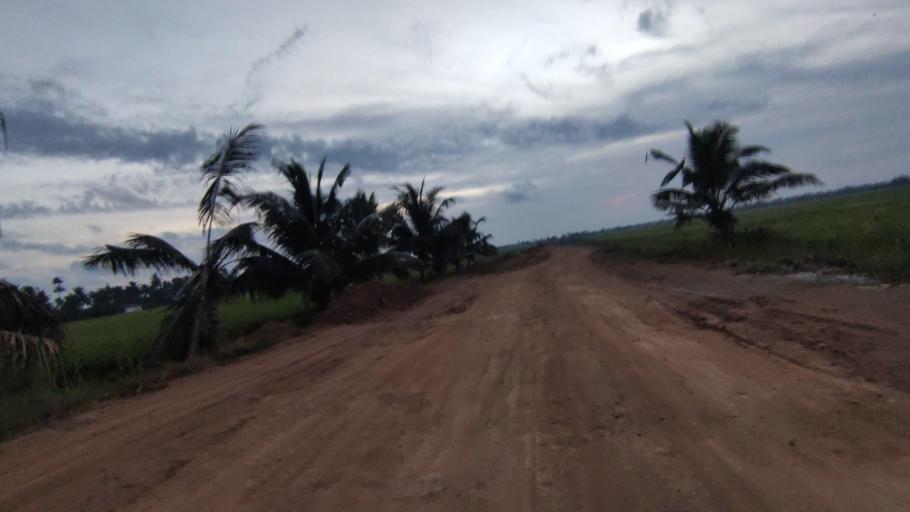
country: IN
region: Kerala
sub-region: Kottayam
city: Kottayam
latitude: 9.6437
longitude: 76.4507
